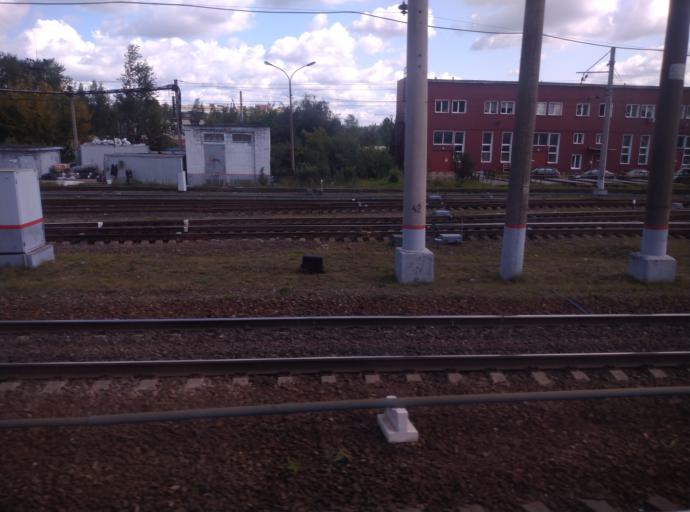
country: RU
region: St.-Petersburg
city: Centralniy
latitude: 59.8948
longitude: 30.3902
